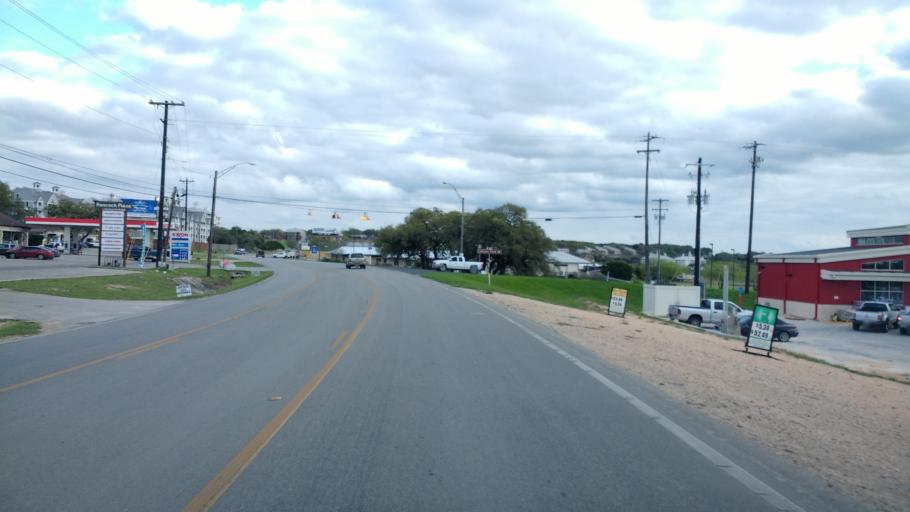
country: US
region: Texas
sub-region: Comal County
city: Canyon Lake
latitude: 29.9148
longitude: -98.2158
